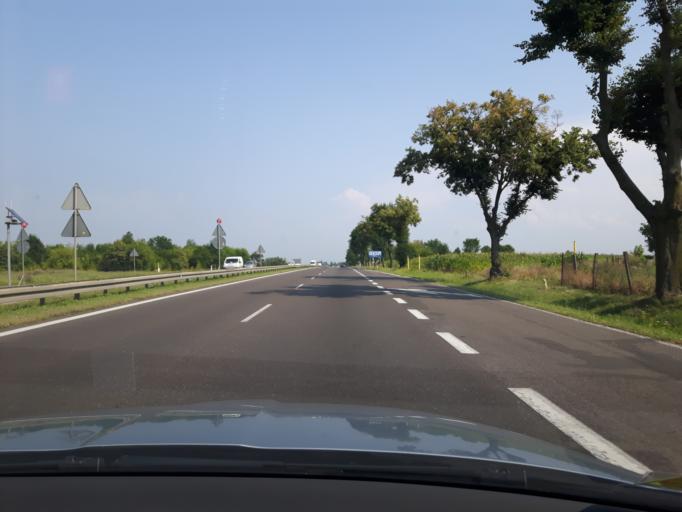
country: PL
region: Masovian Voivodeship
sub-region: Powiat plonski
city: Plonsk
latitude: 52.5996
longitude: 20.4146
